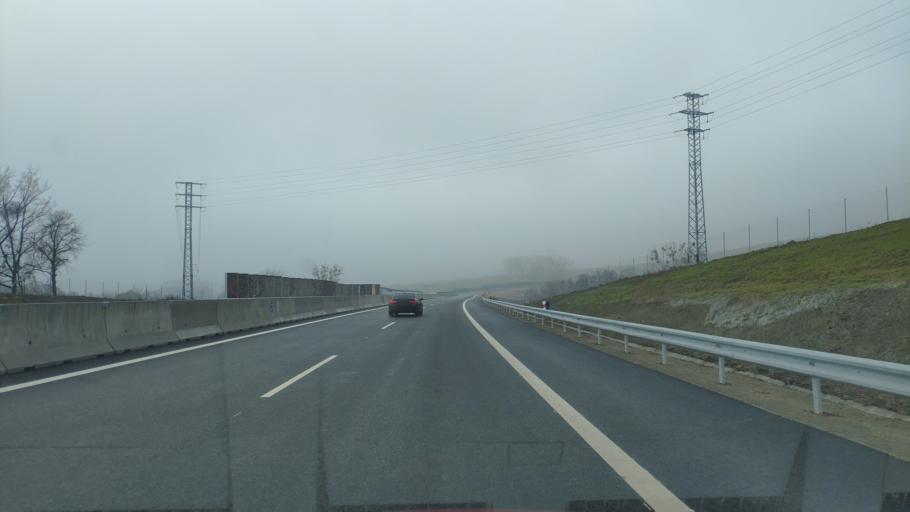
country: SK
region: Kosicky
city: Kosice
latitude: 48.7425
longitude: 21.3687
